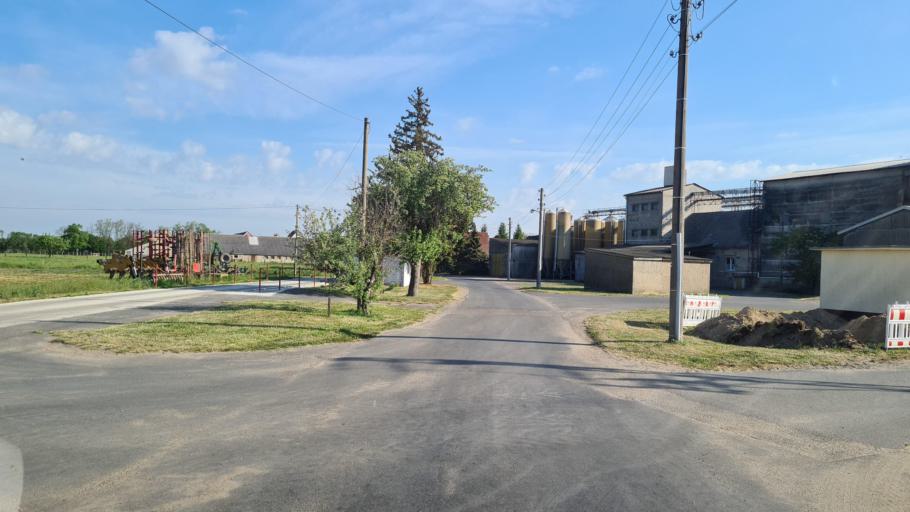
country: DE
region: Brandenburg
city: Falkenberg
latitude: 51.6161
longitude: 13.2058
